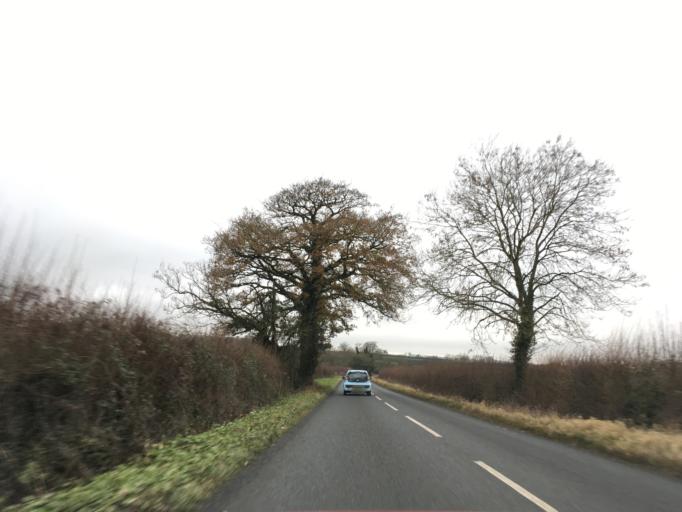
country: GB
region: England
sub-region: Gloucestershire
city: Wotton-under-Edge
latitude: 51.6124
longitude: -2.3466
